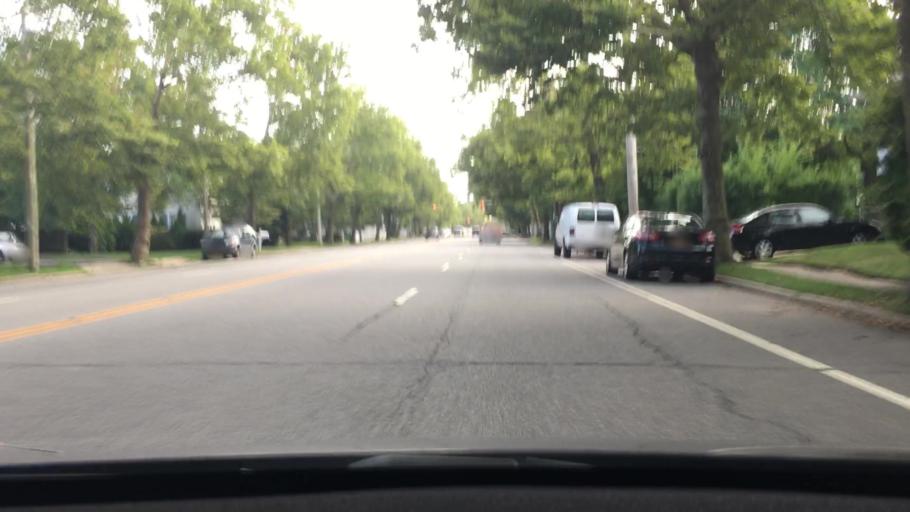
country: US
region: New York
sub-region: Nassau County
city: Hicksville
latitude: 40.7748
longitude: -73.5138
